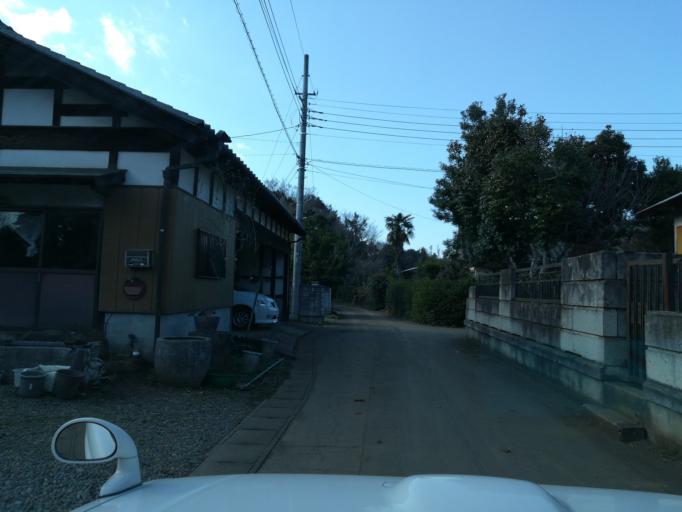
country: JP
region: Ibaraki
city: Naka
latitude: 36.0903
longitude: 140.0888
